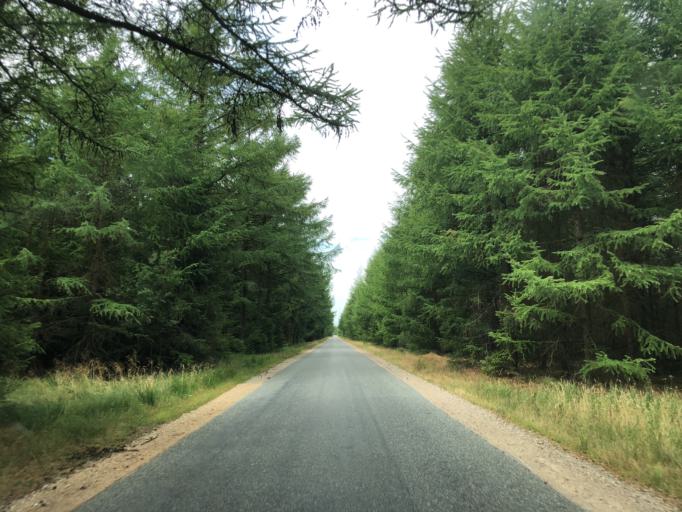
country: DK
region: South Denmark
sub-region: Billund Kommune
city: Grindsted
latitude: 55.6474
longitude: 8.9003
